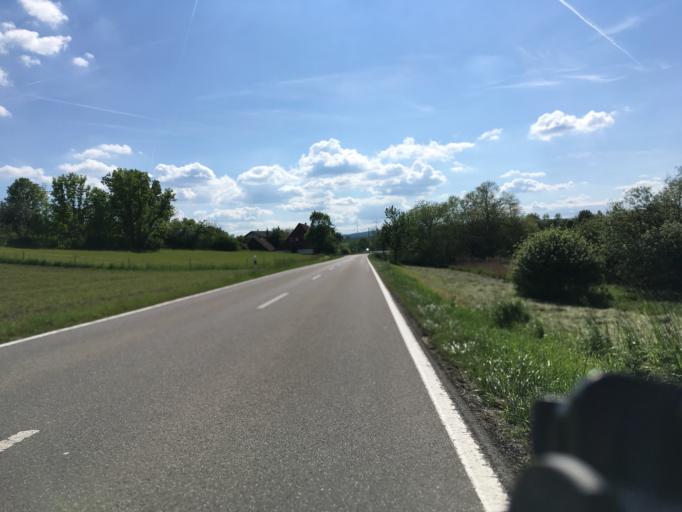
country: CH
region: Schaffhausen
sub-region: Bezirk Reiat
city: Thayngen
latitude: 47.7963
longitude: 8.7210
